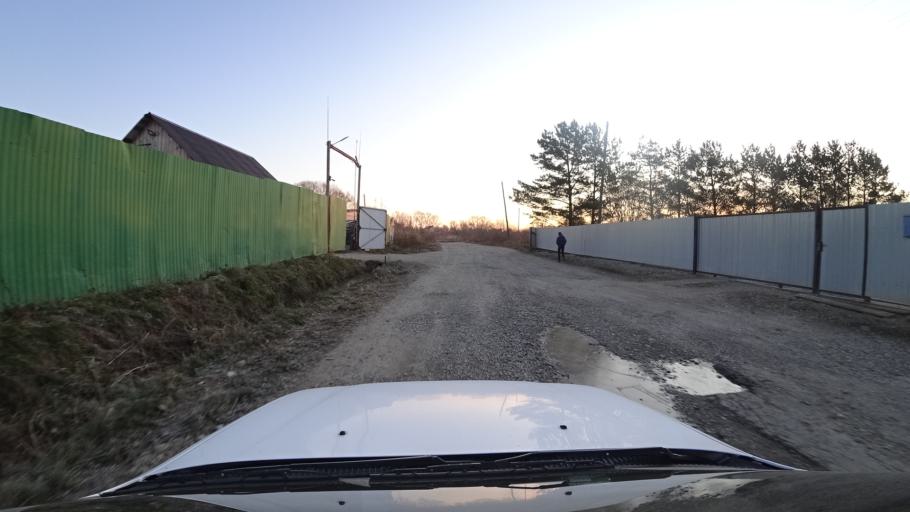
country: RU
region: Primorskiy
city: Dal'nerechensk
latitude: 45.9187
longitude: 133.7367
